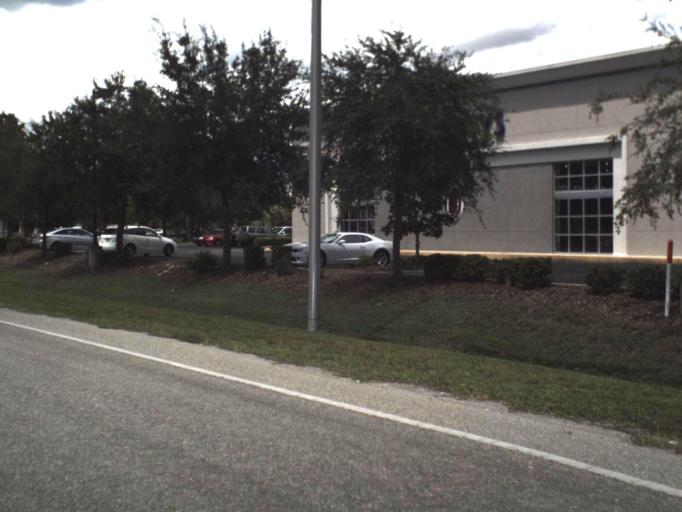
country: US
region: Florida
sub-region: Charlotte County
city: Port Charlotte
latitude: 27.0036
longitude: -82.1283
